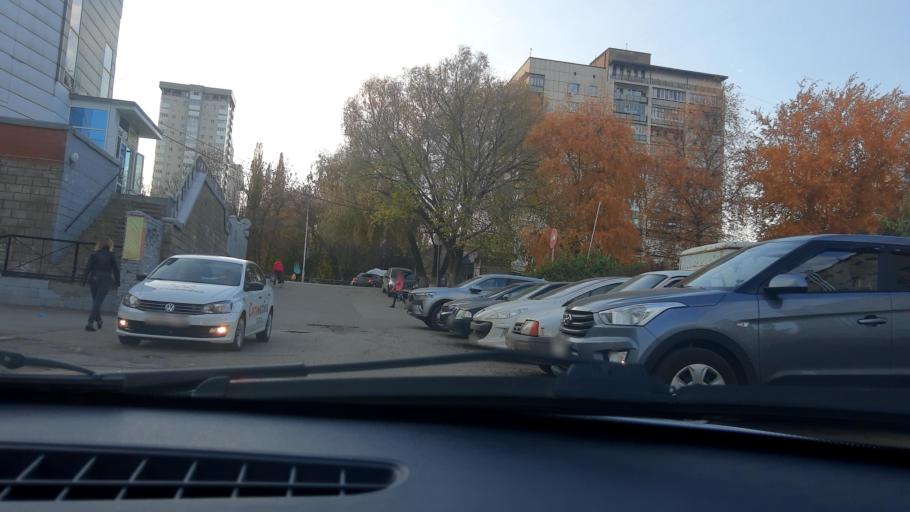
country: RU
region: Bashkortostan
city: Ufa
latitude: 54.7848
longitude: 56.0400
